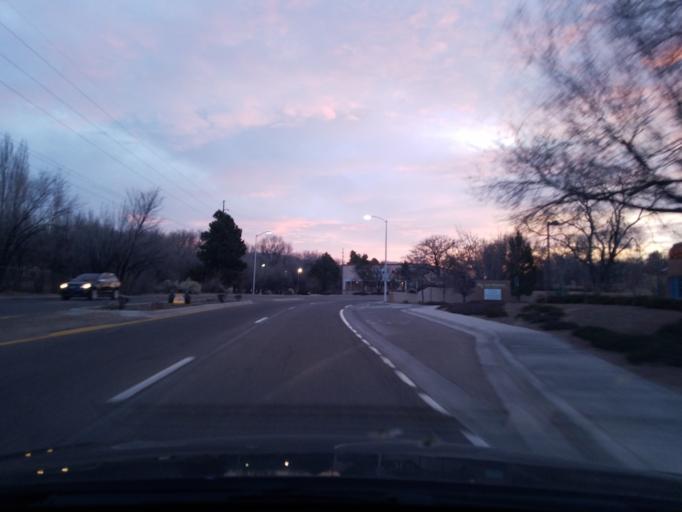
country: US
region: New Mexico
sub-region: Santa Fe County
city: Santa Fe
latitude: 35.6924
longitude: -105.9421
